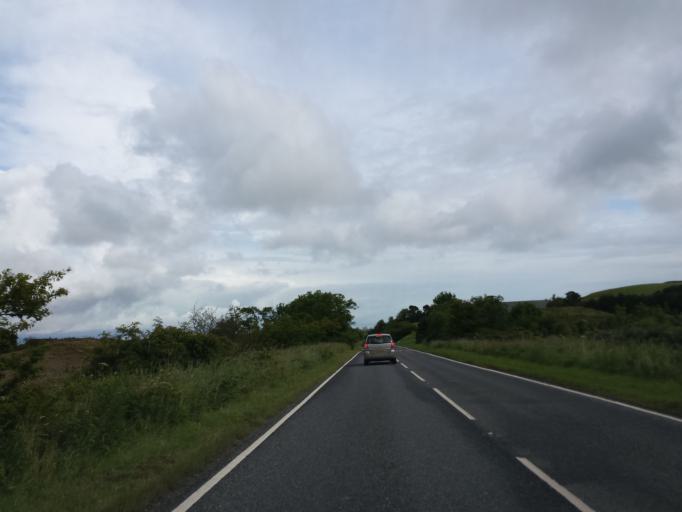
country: GB
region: Scotland
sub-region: Fife
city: Saint Andrews
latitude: 56.3158
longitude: -2.8205
